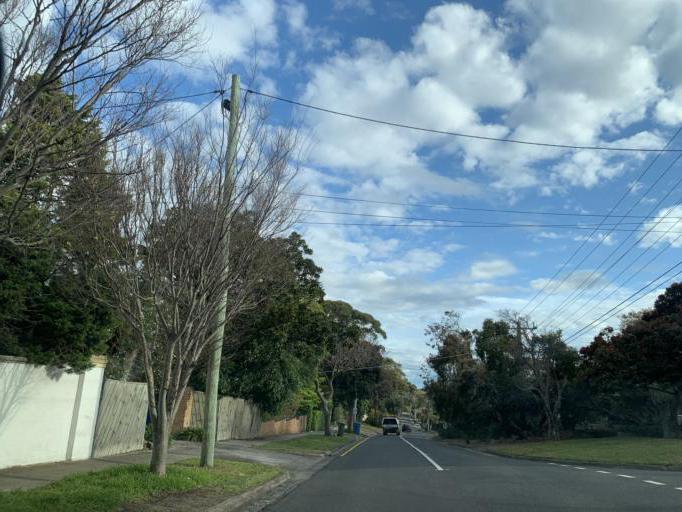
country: AU
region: Victoria
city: Beaumaris
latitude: -37.9791
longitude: 145.0296
